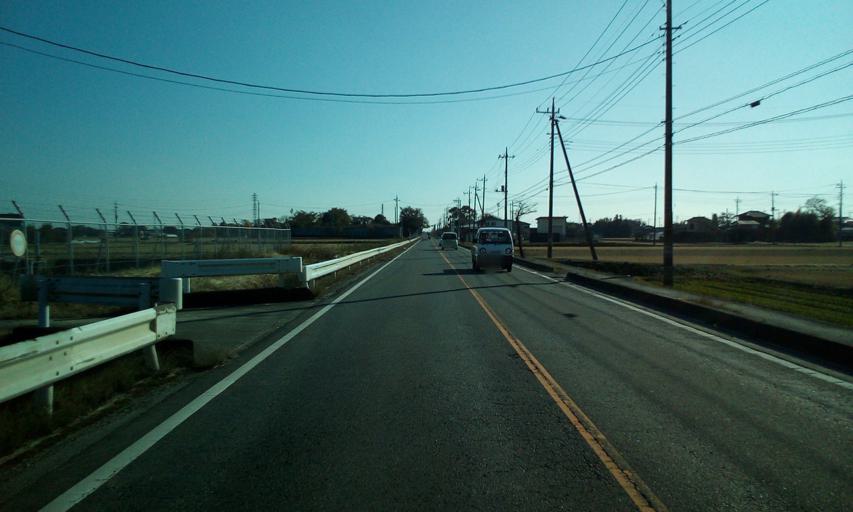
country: JP
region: Saitama
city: Sugito
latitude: 36.0258
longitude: 139.7889
